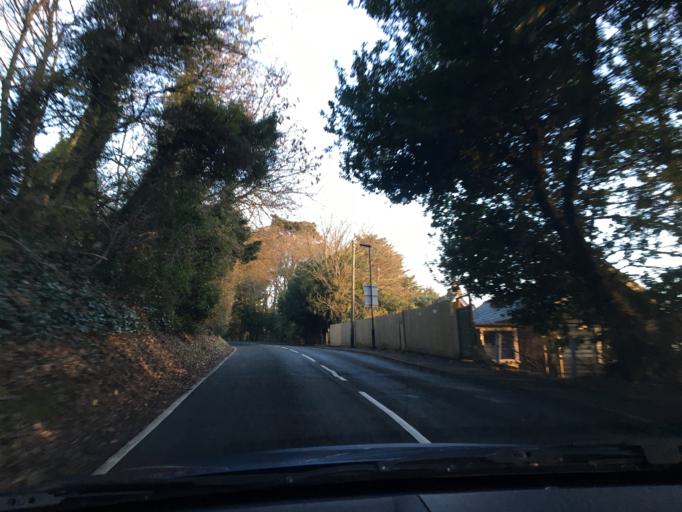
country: GB
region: England
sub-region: Isle of Wight
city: Shanklin
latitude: 50.6052
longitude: -1.1816
